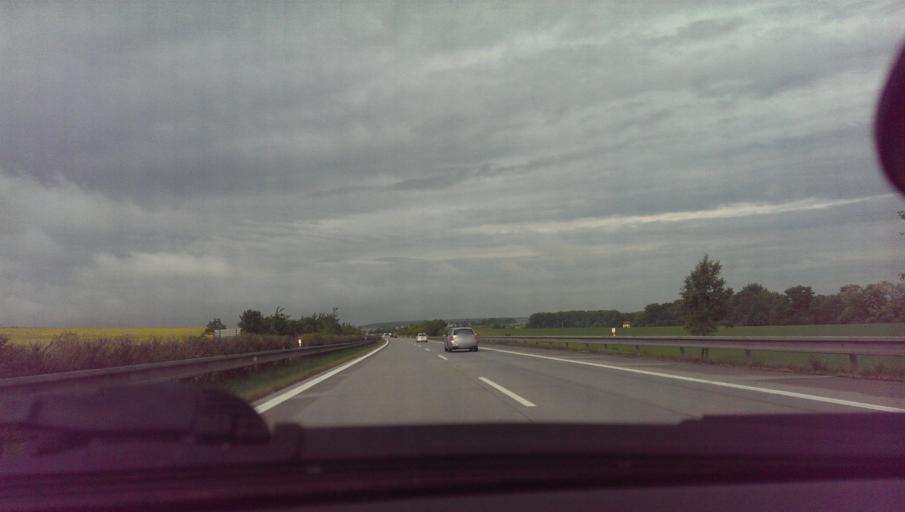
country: CZ
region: South Moravian
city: Ivanovice na Hane
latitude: 49.2867
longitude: 17.0856
